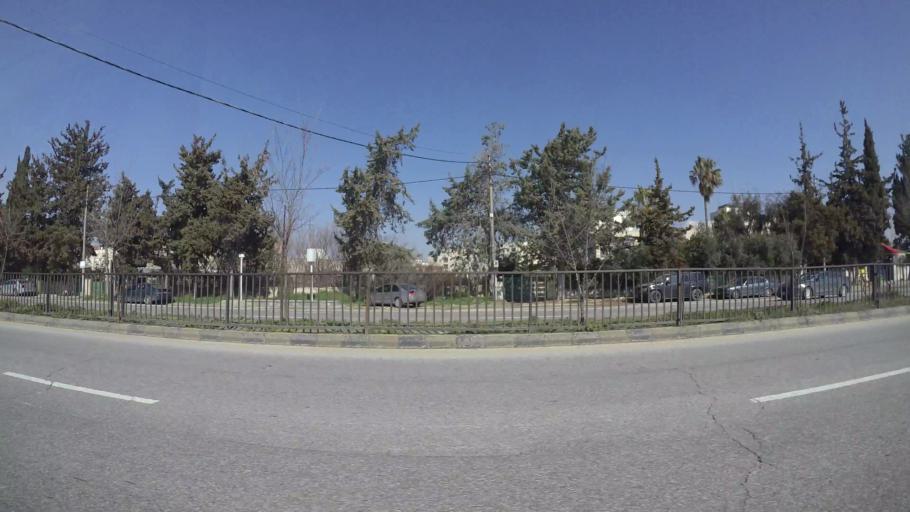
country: JO
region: Amman
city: Al Bunayyat ash Shamaliyah
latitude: 31.9032
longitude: 35.8771
